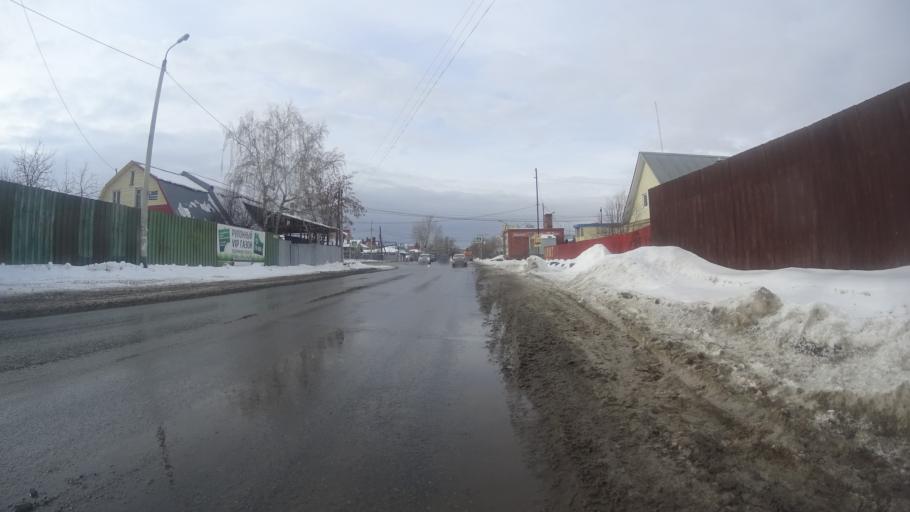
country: RU
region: Chelyabinsk
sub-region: Gorod Chelyabinsk
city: Chelyabinsk
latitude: 55.1313
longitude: 61.3864
